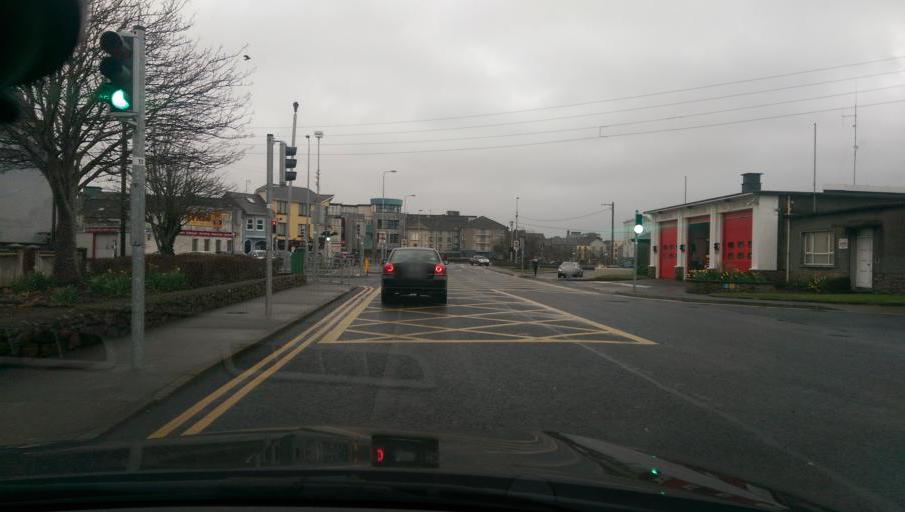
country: IE
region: Connaught
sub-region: County Galway
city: Gaillimh
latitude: 53.2689
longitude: -9.0576
